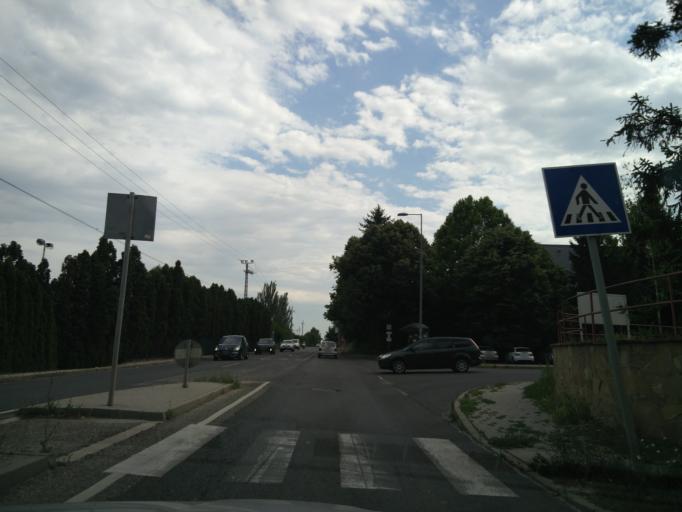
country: HU
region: Pest
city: Toeroekbalint
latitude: 47.4714
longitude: 18.9015
